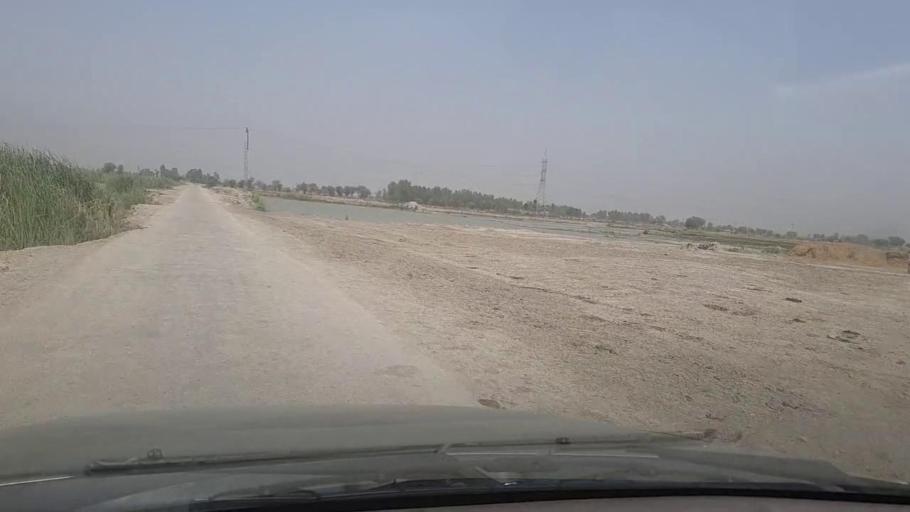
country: PK
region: Sindh
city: Madeji
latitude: 27.8262
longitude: 68.3940
